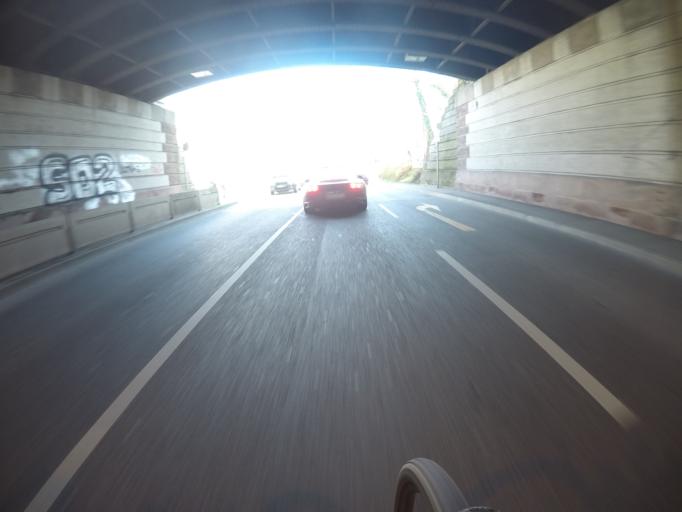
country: DE
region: Baden-Wuerttemberg
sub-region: Regierungsbezirk Stuttgart
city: Stuttgart
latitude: 48.7700
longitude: 9.1426
